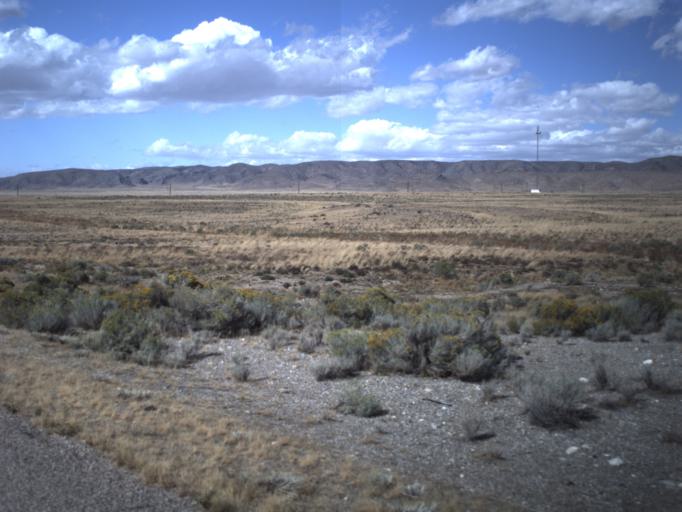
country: US
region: Utah
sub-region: Beaver County
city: Milford
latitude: 38.8066
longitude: -112.8797
